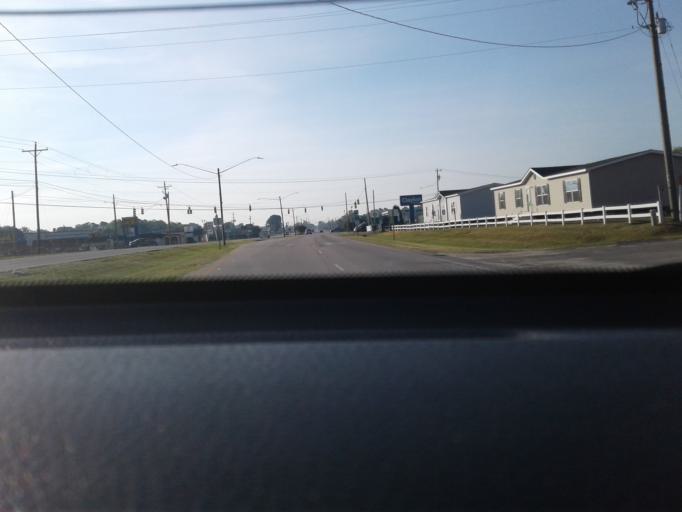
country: US
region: North Carolina
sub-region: Harnett County
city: Dunn
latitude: 35.3193
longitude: -78.6319
